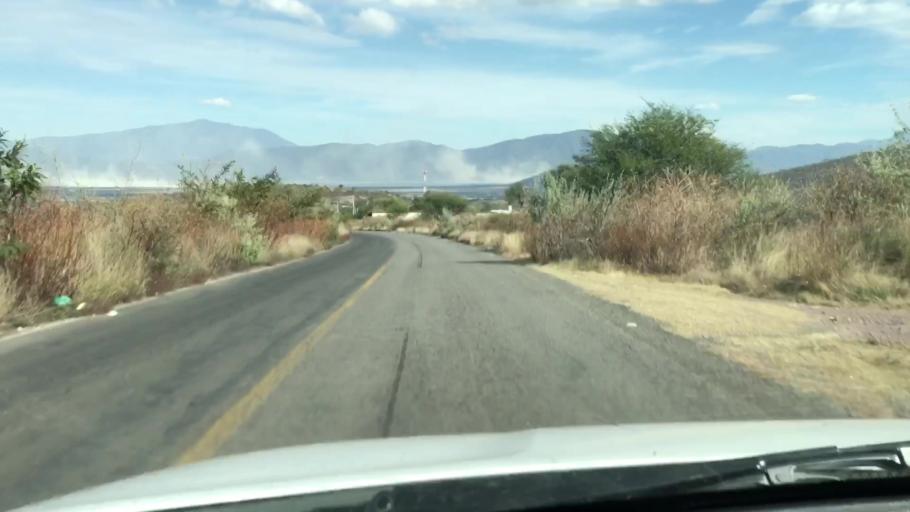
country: MX
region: Jalisco
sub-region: Zacoalco de Torres
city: Barranca de Otates (Barranca de Otatan)
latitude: 20.2566
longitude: -103.6693
